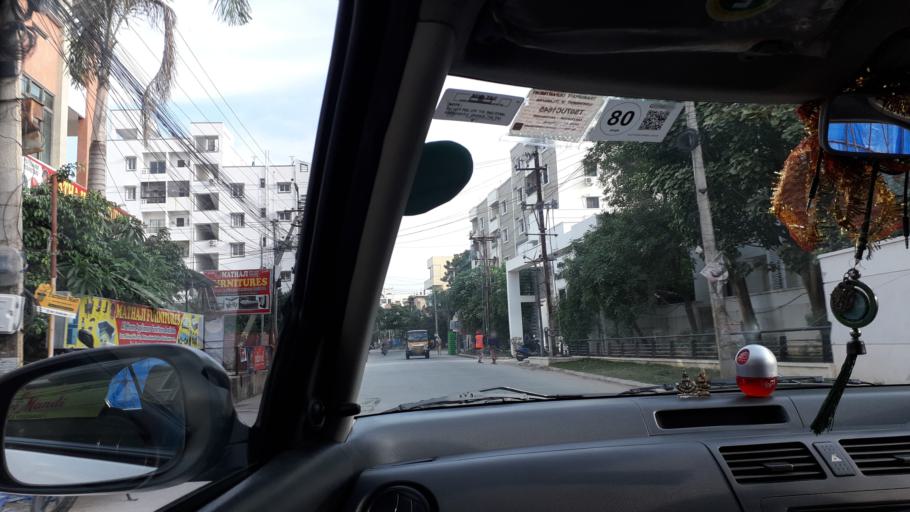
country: IN
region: Telangana
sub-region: Hyderabad
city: Hyderabad
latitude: 17.3977
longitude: 78.3778
